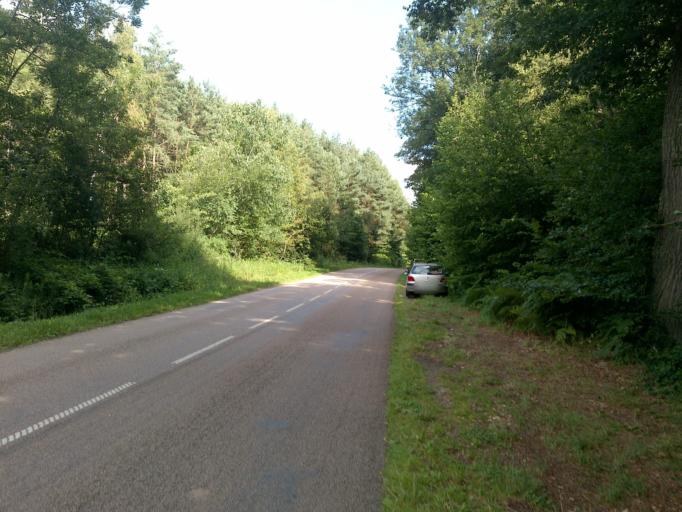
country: FR
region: Lorraine
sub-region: Departement des Vosges
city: Archettes
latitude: 48.1202
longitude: 6.5536
